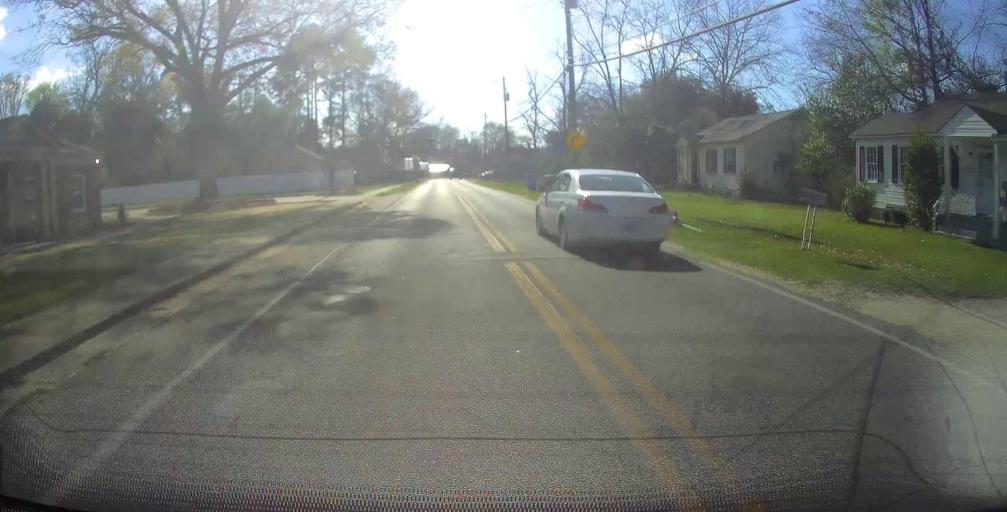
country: US
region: Georgia
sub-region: Laurens County
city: Dublin
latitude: 32.5434
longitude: -82.9114
